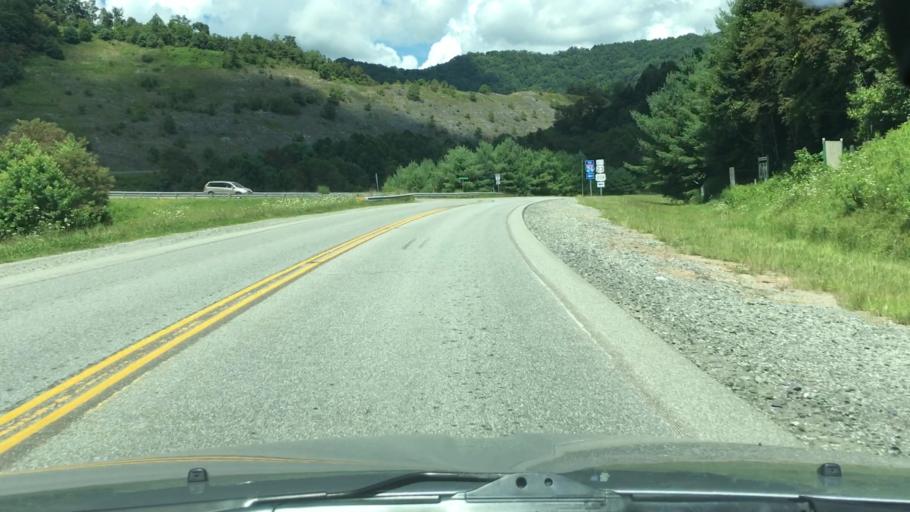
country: US
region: North Carolina
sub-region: Madison County
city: Mars Hill
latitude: 35.9094
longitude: -82.5549
